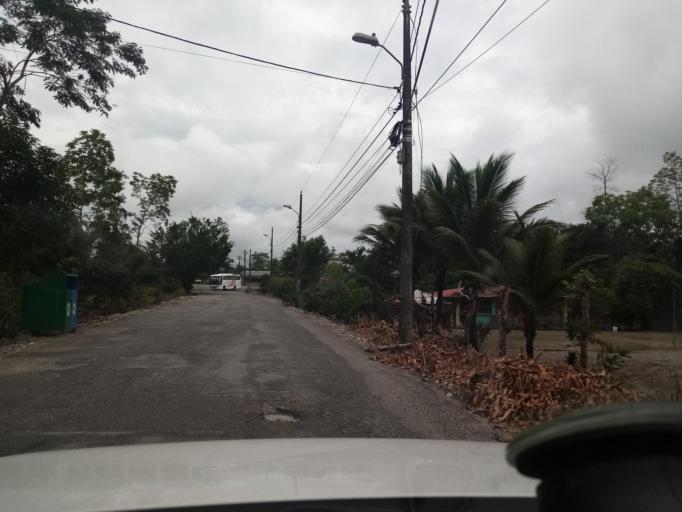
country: EC
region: Napo
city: Tena
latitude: -1.0468
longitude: -77.7954
